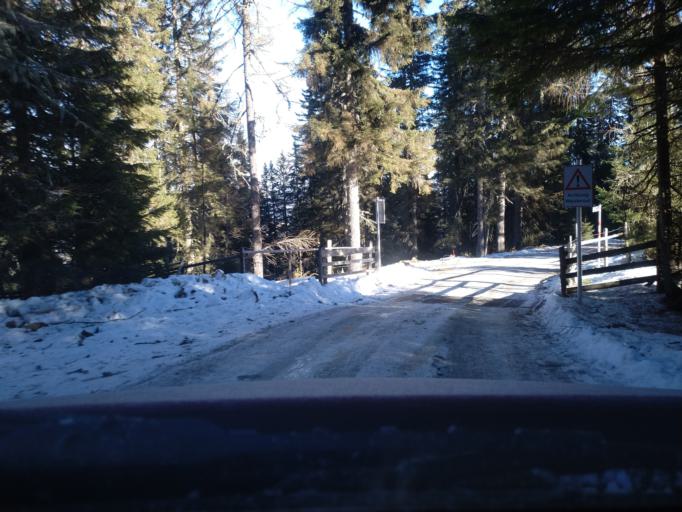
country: AT
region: Carinthia
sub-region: Politischer Bezirk Villach Land
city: Arriach
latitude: 46.6995
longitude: 13.8952
